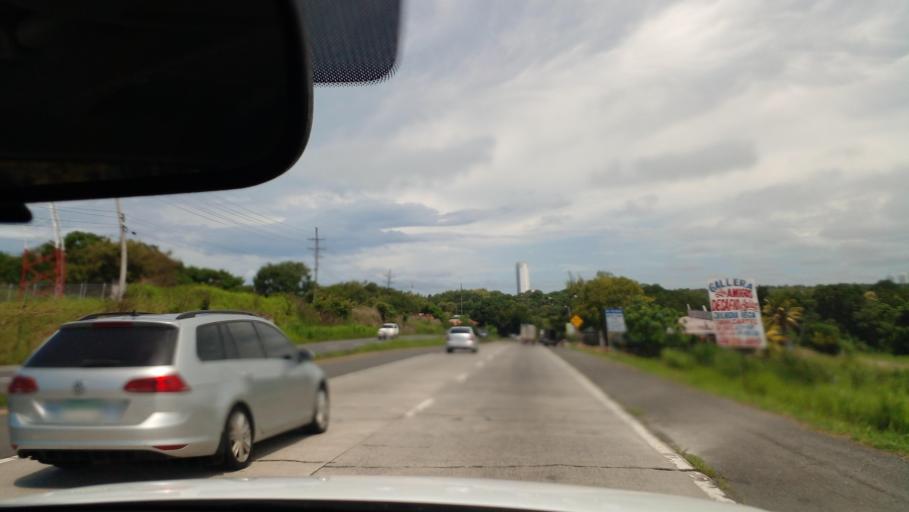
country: PA
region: Panama
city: Nueva Gorgona
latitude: 8.4809
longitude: -79.9583
